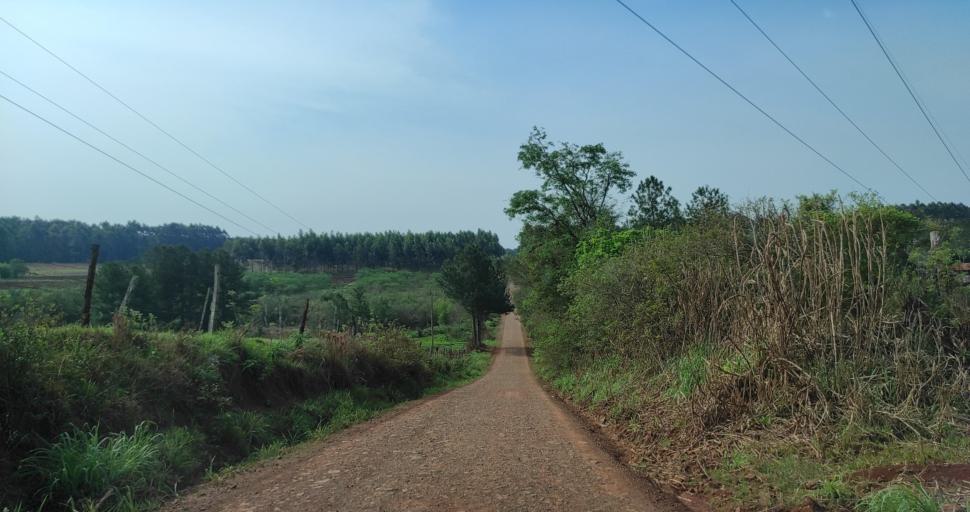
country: AR
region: Misiones
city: Garuhape
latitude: -26.8724
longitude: -55.0057
